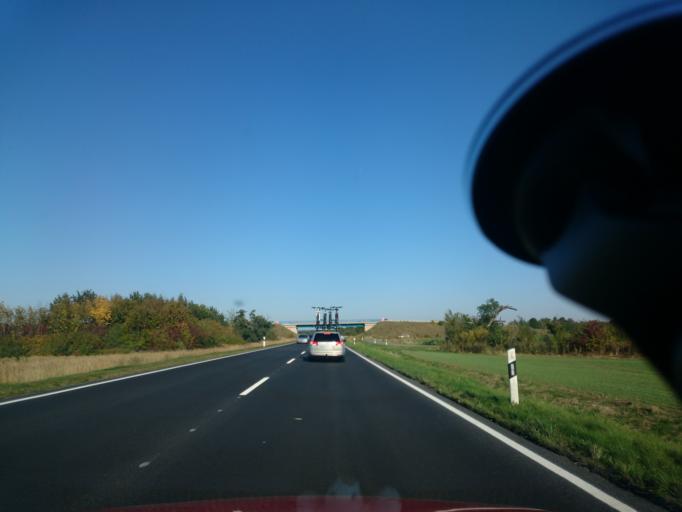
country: DE
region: Mecklenburg-Vorpommern
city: Bentwisch
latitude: 54.1244
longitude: 12.2041
